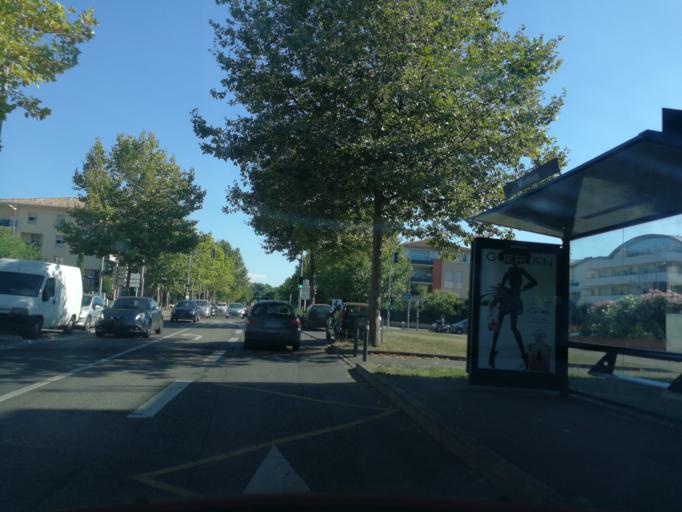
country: FR
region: Midi-Pyrenees
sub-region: Departement de la Haute-Garonne
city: Toulouse
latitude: 43.6376
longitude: 1.4527
